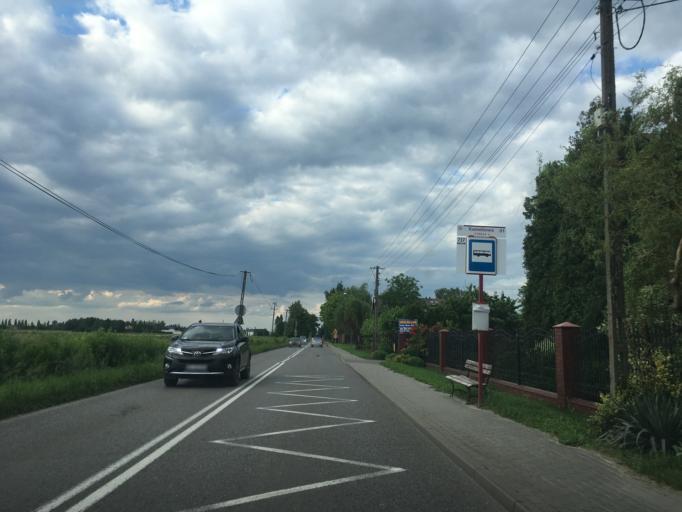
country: PL
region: Masovian Voivodeship
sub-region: Powiat piaseczynski
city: Lesznowola
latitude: 52.0964
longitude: 20.9737
